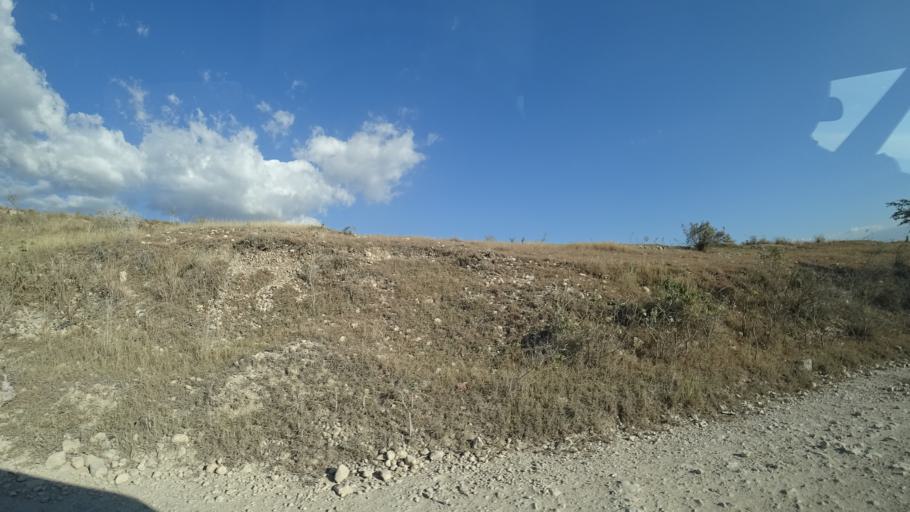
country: HT
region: Ouest
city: Cabaret
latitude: 18.6815
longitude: -72.3189
